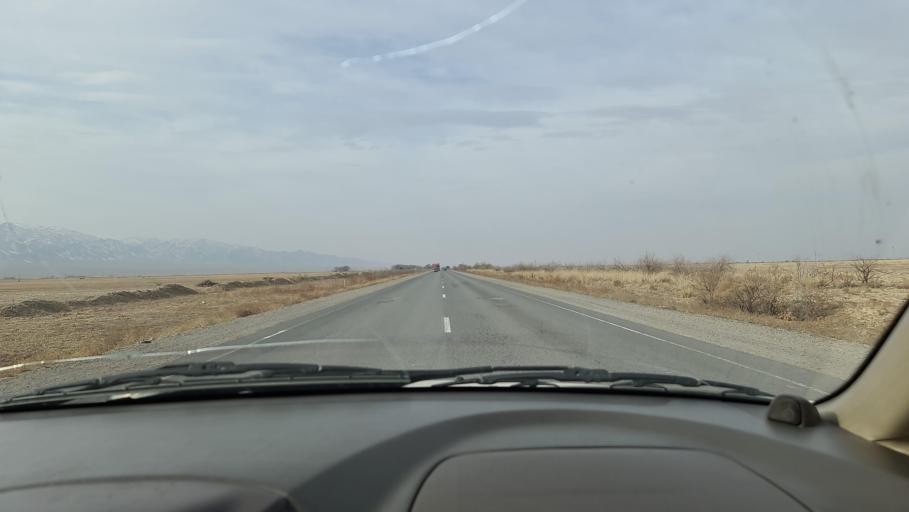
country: KG
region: Chuy
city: Tokmok
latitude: 43.3474
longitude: 75.5004
